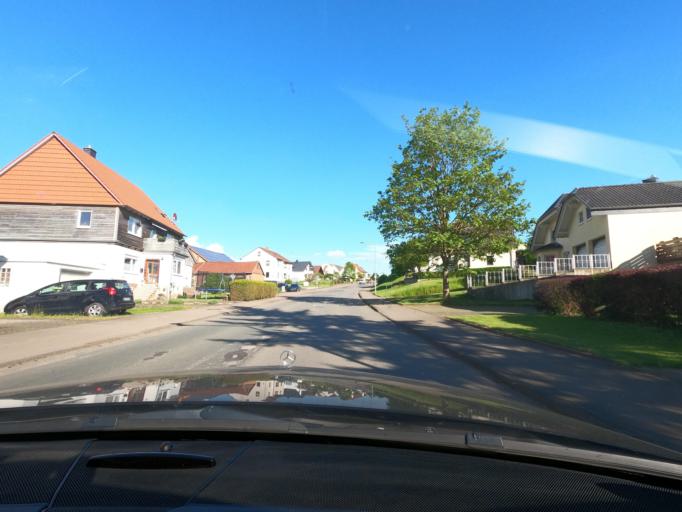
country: DE
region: Hesse
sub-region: Regierungsbezirk Kassel
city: Breuna
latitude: 51.3871
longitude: 9.1937
